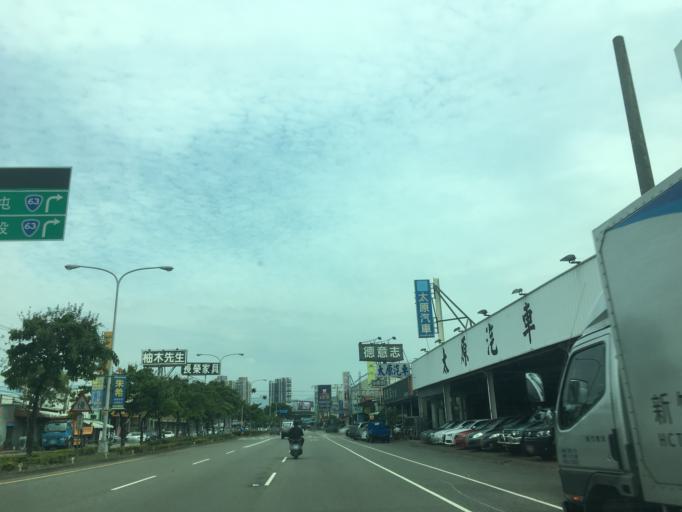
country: TW
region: Taiwan
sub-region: Taichung City
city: Taichung
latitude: 24.1040
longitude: 120.6688
